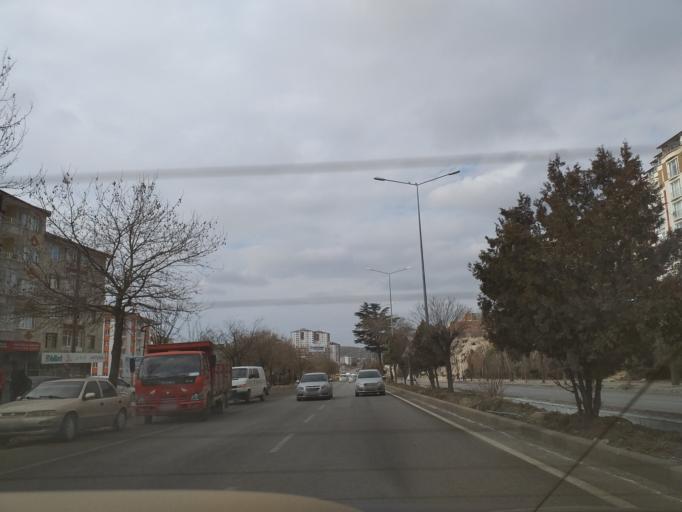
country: TR
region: Yozgat
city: Yozgat
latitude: 39.8194
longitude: 34.8018
